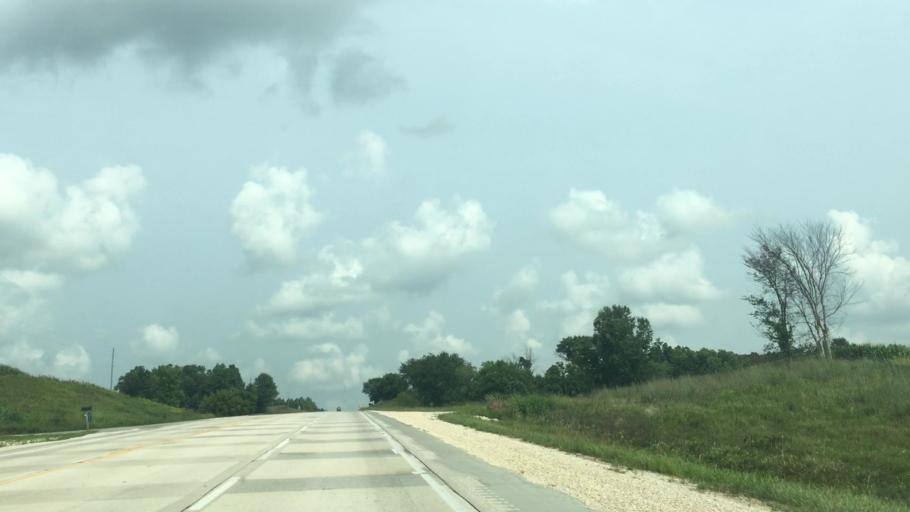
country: US
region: Iowa
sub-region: Winneshiek County
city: Decorah
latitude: 43.3293
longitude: -91.8130
